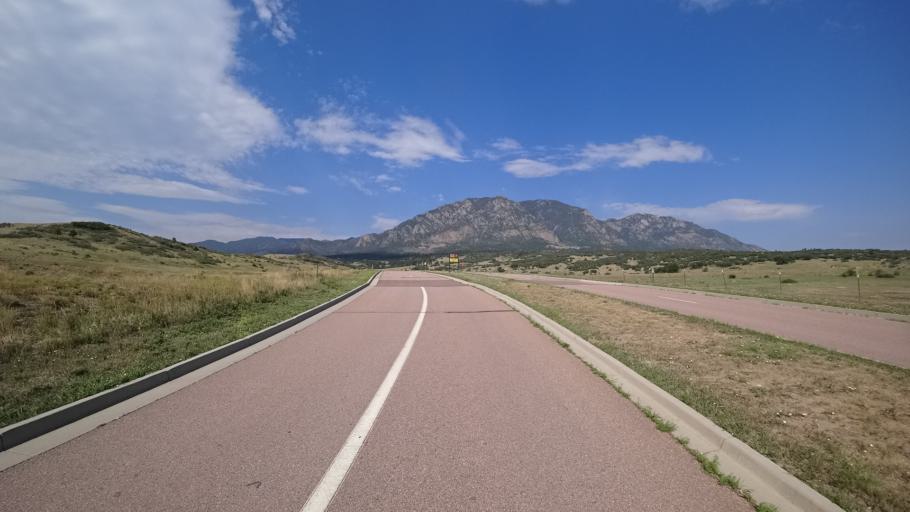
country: US
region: Colorado
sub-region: El Paso County
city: Fort Carson
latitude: 38.7381
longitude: -104.8095
